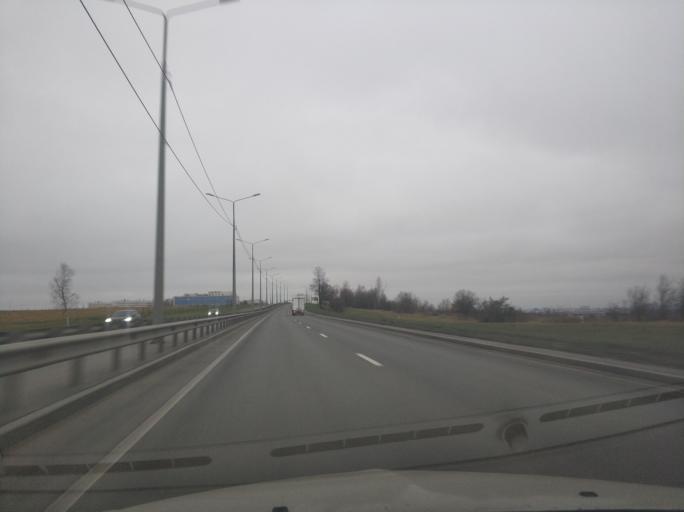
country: RU
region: St.-Petersburg
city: Pushkin
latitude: 59.7575
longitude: 30.3777
